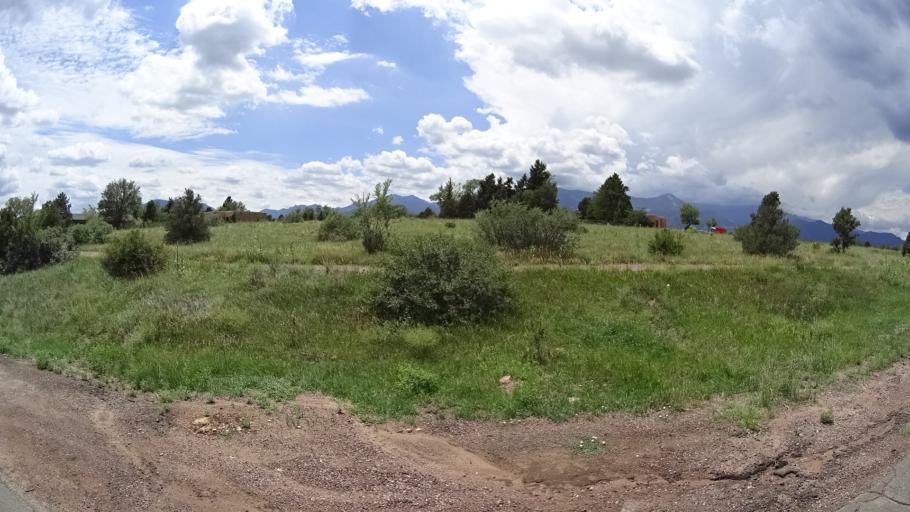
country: US
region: Colorado
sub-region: El Paso County
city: Colorado Springs
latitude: 38.8545
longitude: -104.8437
